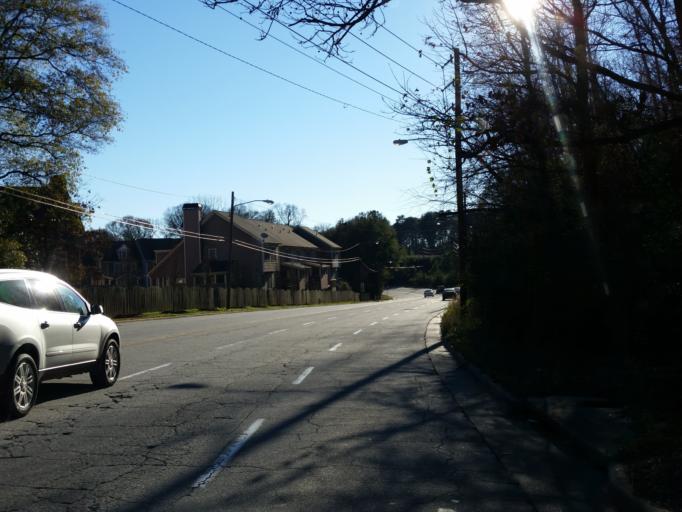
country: US
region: Georgia
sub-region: Fulton County
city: Atlanta
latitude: 33.7844
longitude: -84.4282
